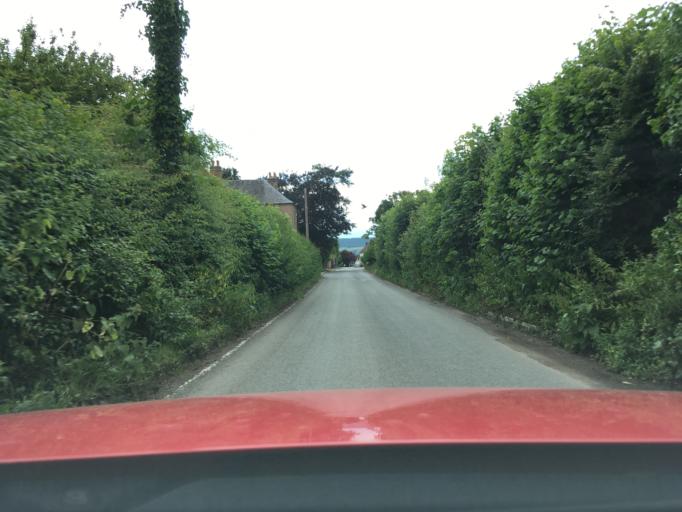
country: GB
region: England
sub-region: Gloucestershire
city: Cinderford
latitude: 51.7960
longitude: -2.4216
